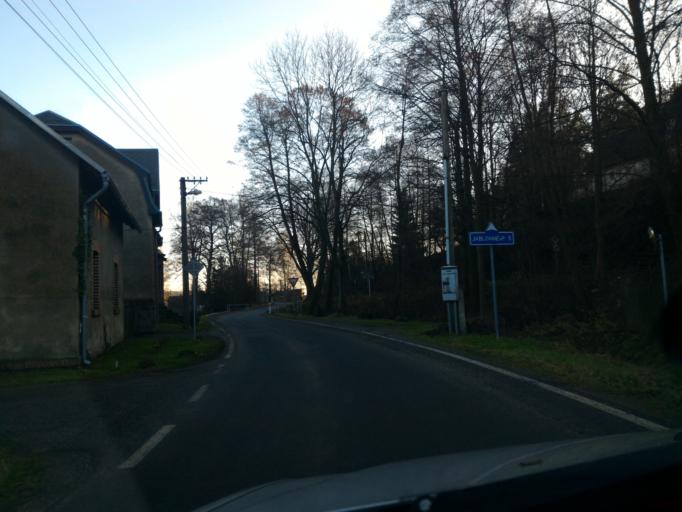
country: DE
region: Saxony
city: Kurort Oybin
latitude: 50.7967
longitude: 14.7213
